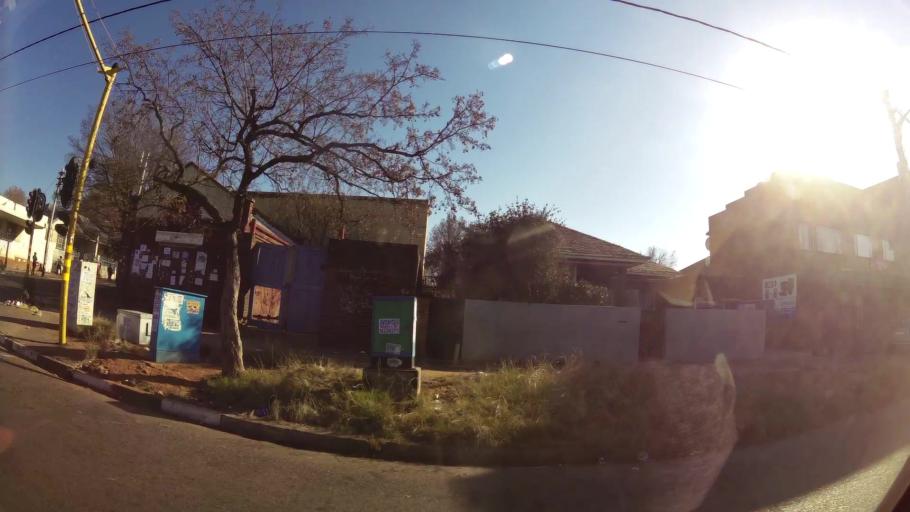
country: ZA
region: Gauteng
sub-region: City of Johannesburg Metropolitan Municipality
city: Johannesburg
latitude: -26.2031
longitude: 28.0991
